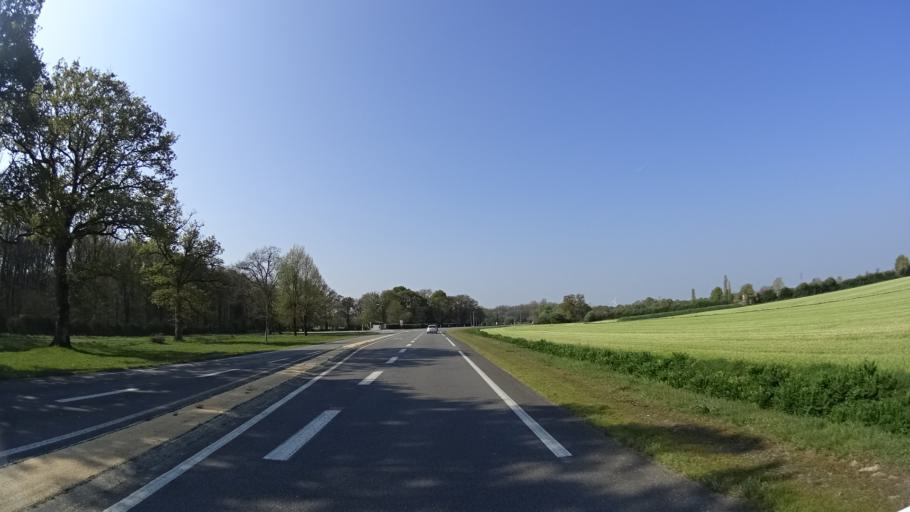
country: FR
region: Pays de la Loire
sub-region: Departement de la Loire-Atlantique
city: Sainte-Pazanne
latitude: 47.0911
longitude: -1.8342
